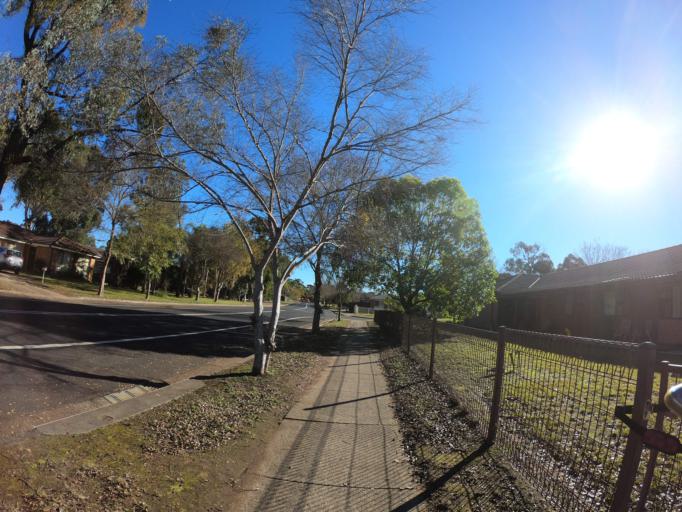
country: AU
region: New South Wales
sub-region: Hawkesbury
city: South Windsor
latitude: -33.6383
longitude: 150.7904
